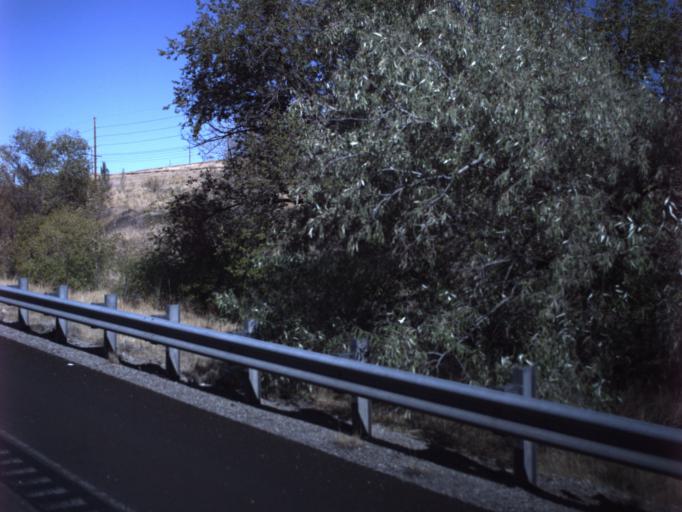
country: US
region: Utah
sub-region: Salt Lake County
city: Magna
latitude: 40.7173
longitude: -112.1354
